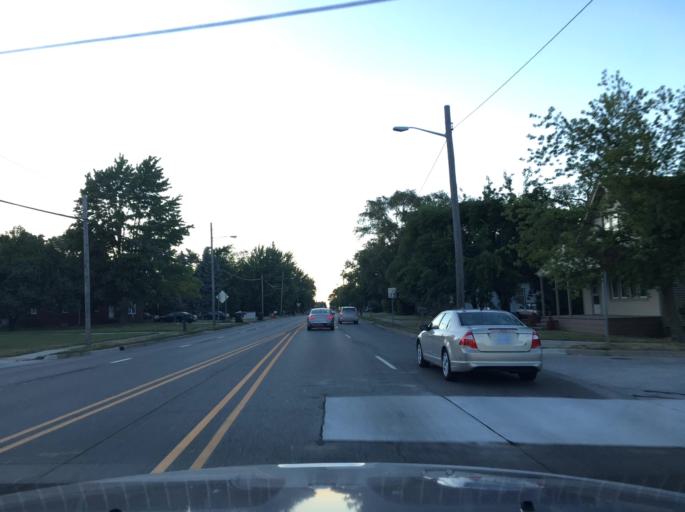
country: US
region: Michigan
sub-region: Macomb County
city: Roseville
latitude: 42.5107
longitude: -82.9366
